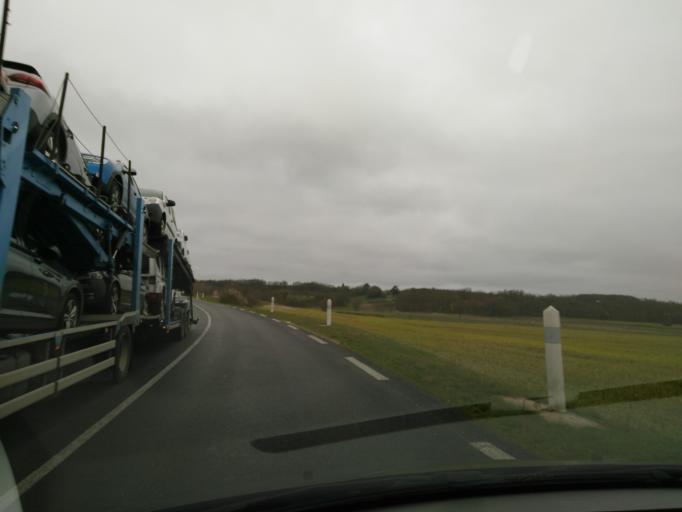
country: FR
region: Aquitaine
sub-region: Departement du Lot-et-Garonne
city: Castillonnes
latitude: 44.7207
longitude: 0.5579
